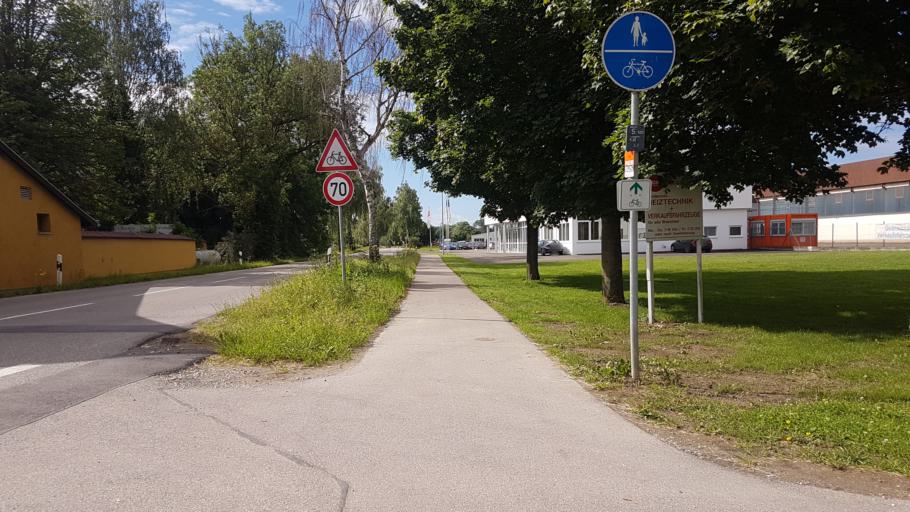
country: DE
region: Bavaria
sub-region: Swabia
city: Guenzburg
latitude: 48.4775
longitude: 10.2609
